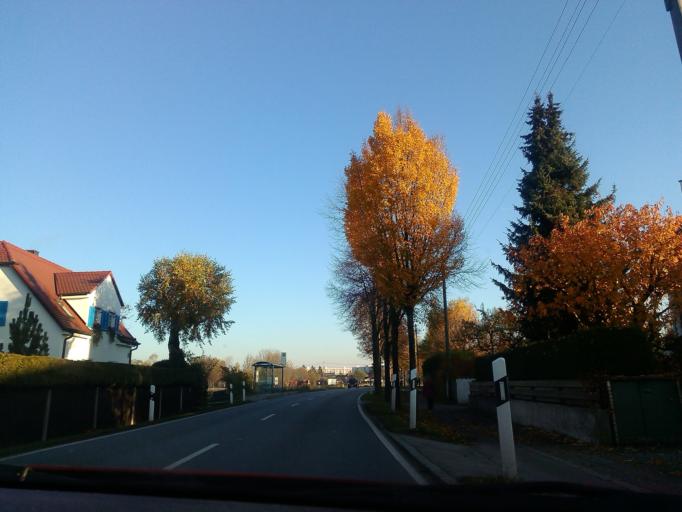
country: DE
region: Bavaria
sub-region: Upper Bavaria
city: Pasing
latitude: 48.1325
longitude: 11.4687
